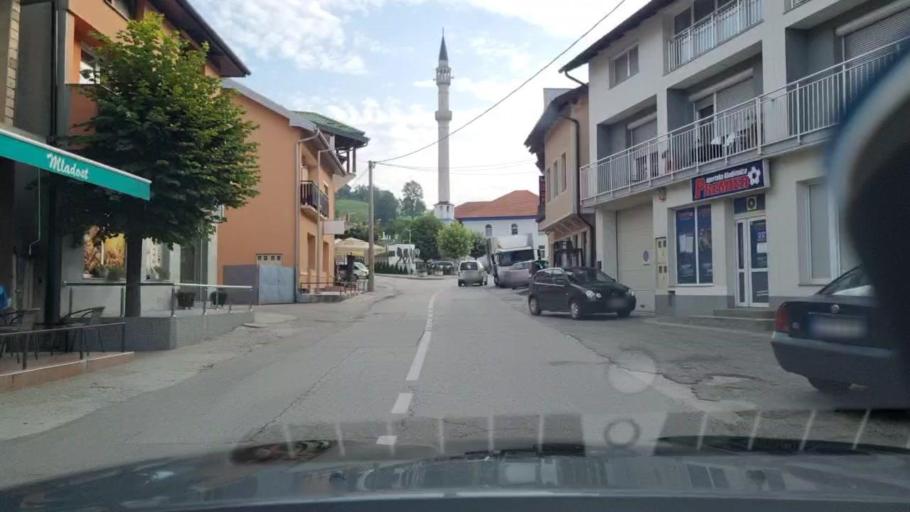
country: BA
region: Federation of Bosnia and Herzegovina
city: Vrnograc
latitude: 45.1628
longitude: 15.9529
